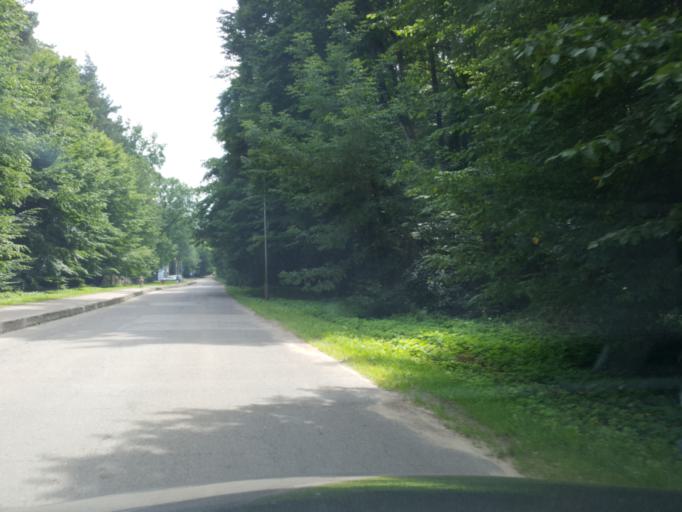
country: LT
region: Alytaus apskritis
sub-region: Alytus
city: Alytus
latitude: 54.3838
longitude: 24.0418
